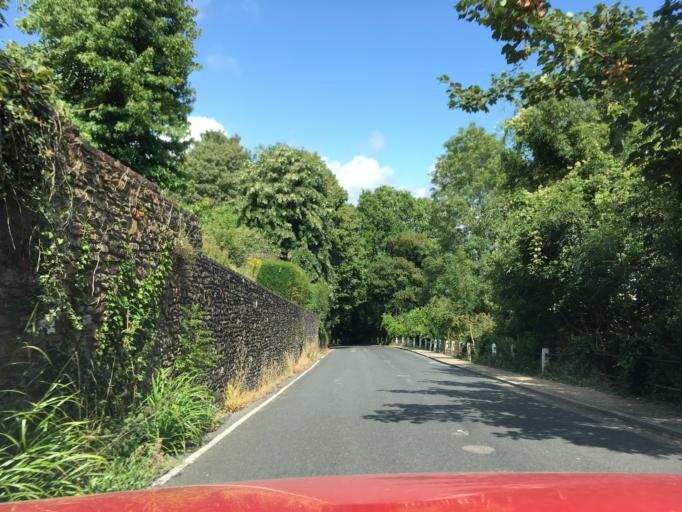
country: GB
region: England
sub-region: East Sussex
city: Rye
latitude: 50.9250
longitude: 0.7121
